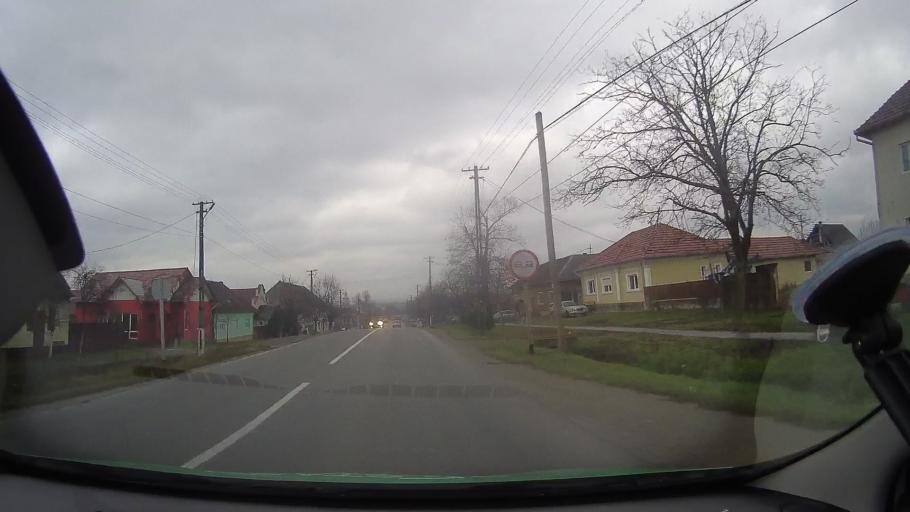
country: RO
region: Arad
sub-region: Comuna Almas
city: Almas
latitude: 46.2861
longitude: 22.2319
